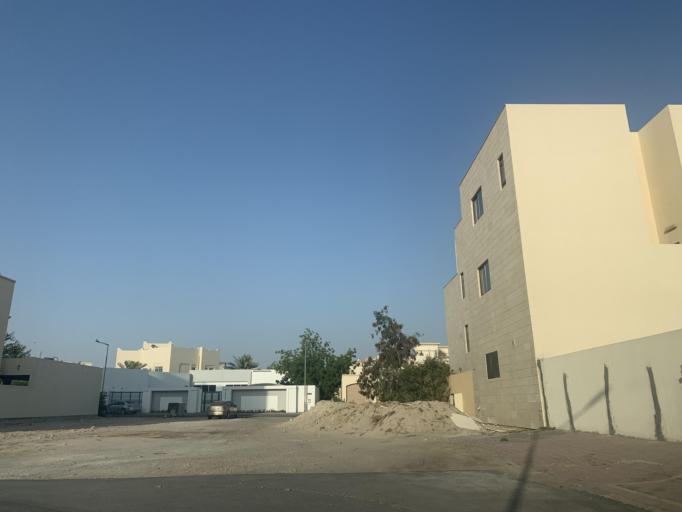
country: BH
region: Manama
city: Jidd Hafs
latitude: 26.2082
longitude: 50.5288
